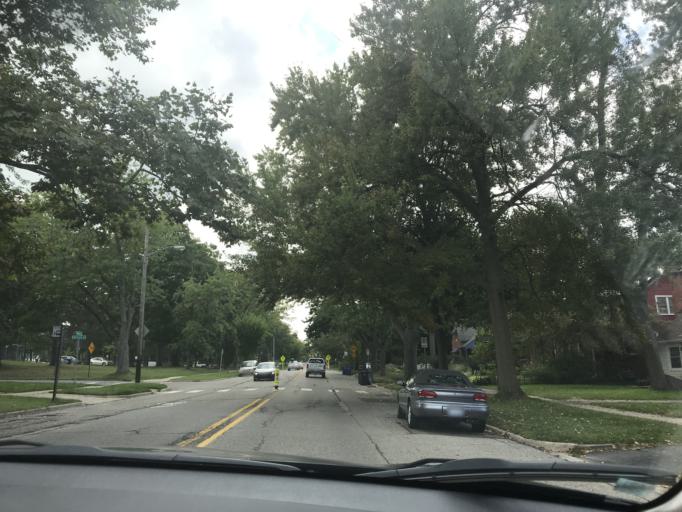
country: US
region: Michigan
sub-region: Washtenaw County
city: Ann Arbor
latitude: 42.2685
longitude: -83.7541
